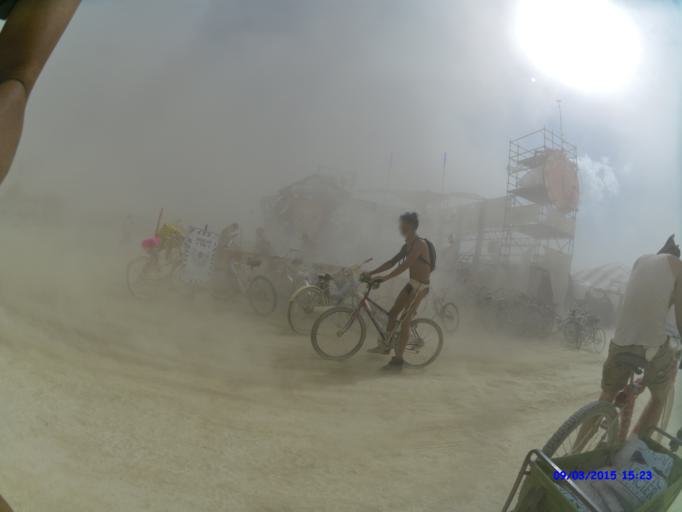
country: US
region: Nevada
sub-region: Pershing County
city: Lovelock
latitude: 40.7777
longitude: -119.2066
